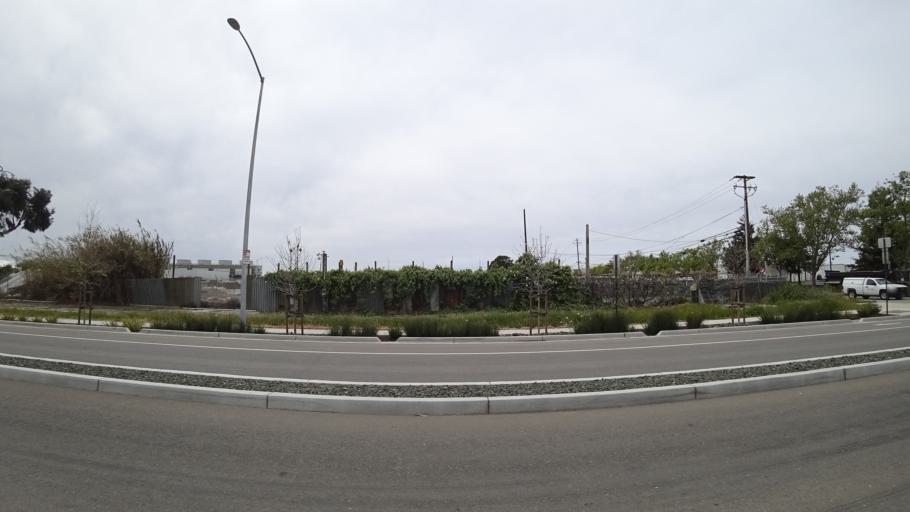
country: US
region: California
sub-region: Alameda County
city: San Lorenzo
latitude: 37.6376
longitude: -122.1329
